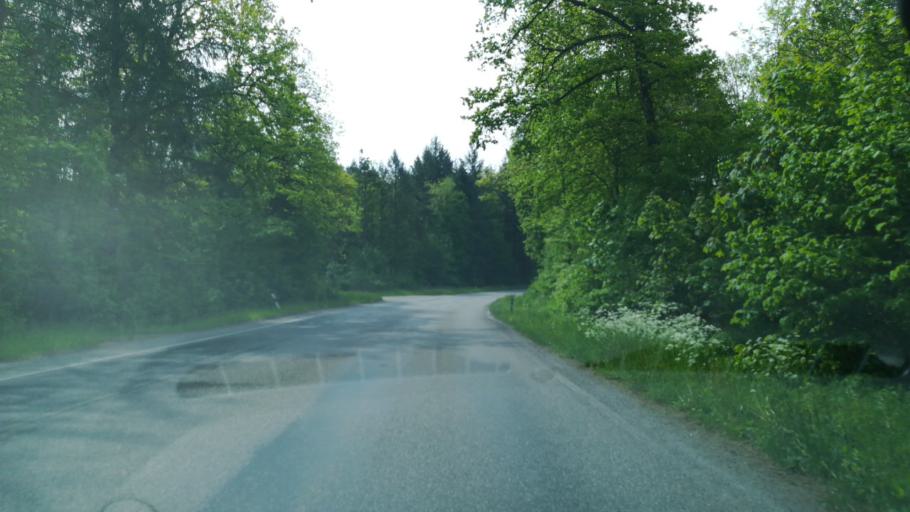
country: DE
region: Baden-Wuerttemberg
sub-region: Freiburg Region
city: Steisslingen
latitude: 47.7710
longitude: 8.8925
